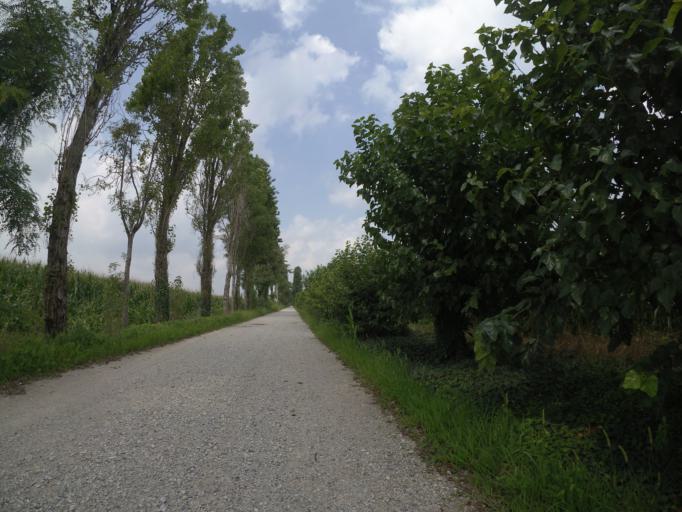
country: IT
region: Friuli Venezia Giulia
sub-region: Provincia di Udine
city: Sedegliano
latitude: 46.0159
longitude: 13.0106
